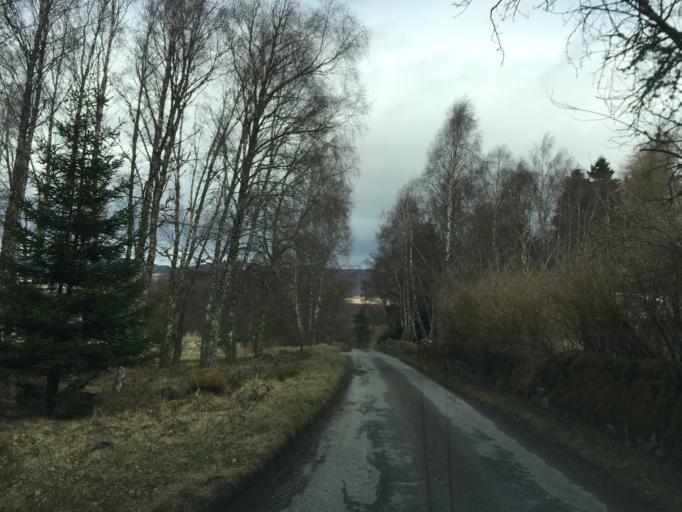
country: GB
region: Scotland
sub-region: Highland
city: Aviemore
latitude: 57.1085
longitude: -3.9206
